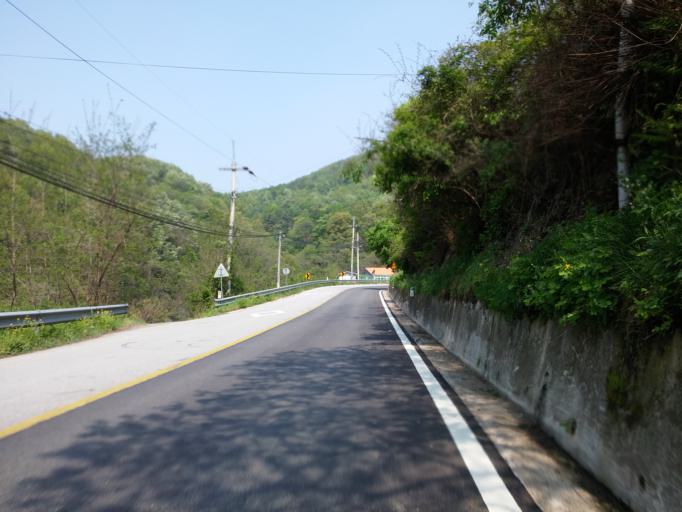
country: KR
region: Chungcheongbuk-do
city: Okcheon
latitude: 36.3978
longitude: 127.6074
